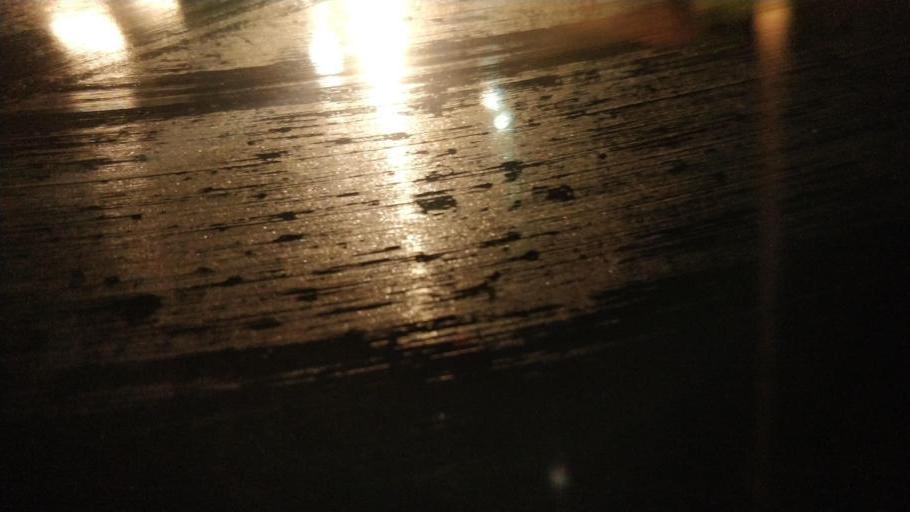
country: IN
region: Kerala
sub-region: Kottayam
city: Kottayam
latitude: 9.6295
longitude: 76.5332
